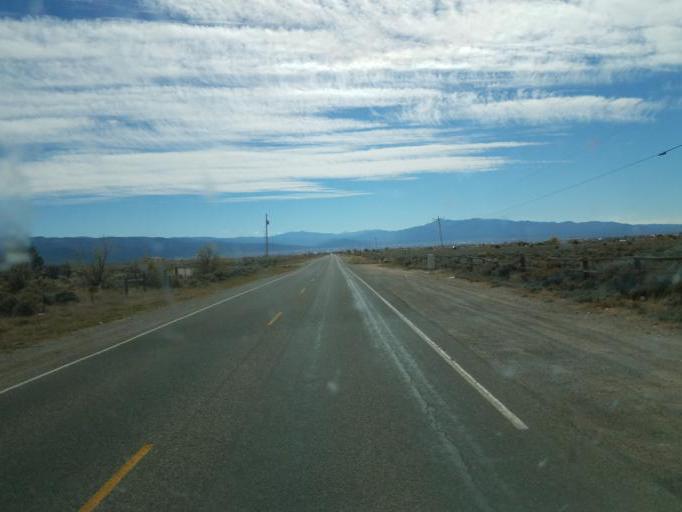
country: US
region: New Mexico
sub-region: Taos County
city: Arroyo Seco
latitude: 36.4868
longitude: -105.5938
